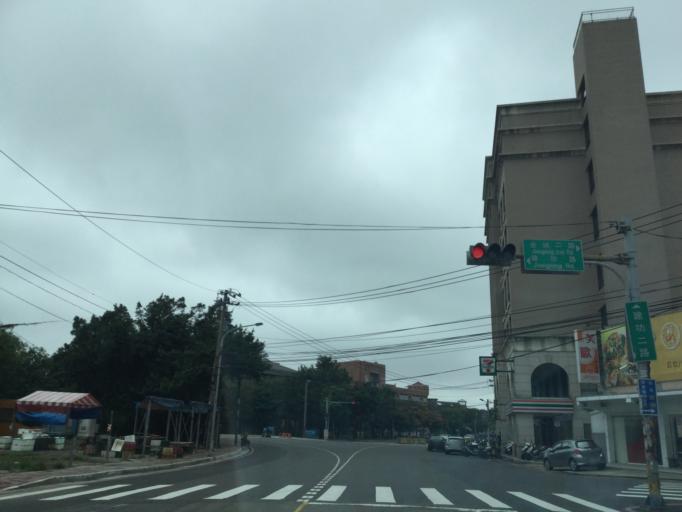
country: TW
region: Taiwan
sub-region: Hsinchu
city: Hsinchu
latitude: 24.7958
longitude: 121.0020
